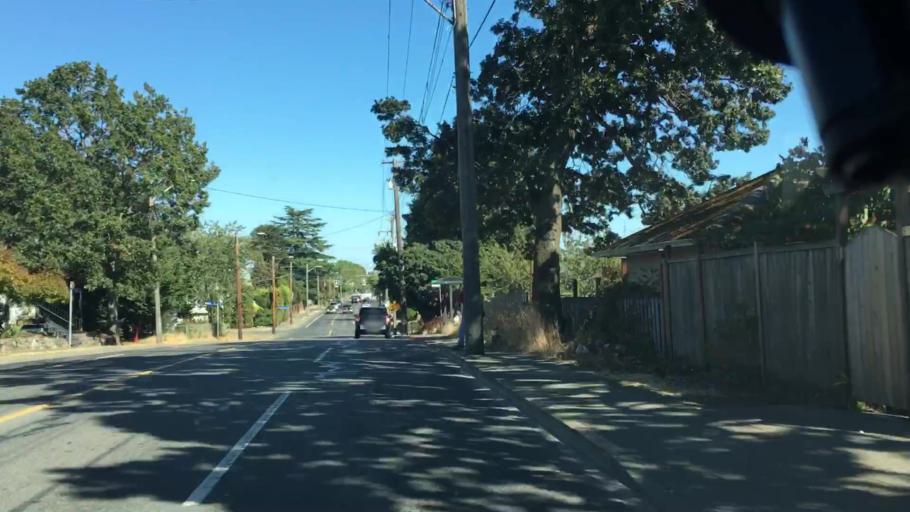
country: CA
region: British Columbia
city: Victoria
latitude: 48.4352
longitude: -123.3574
